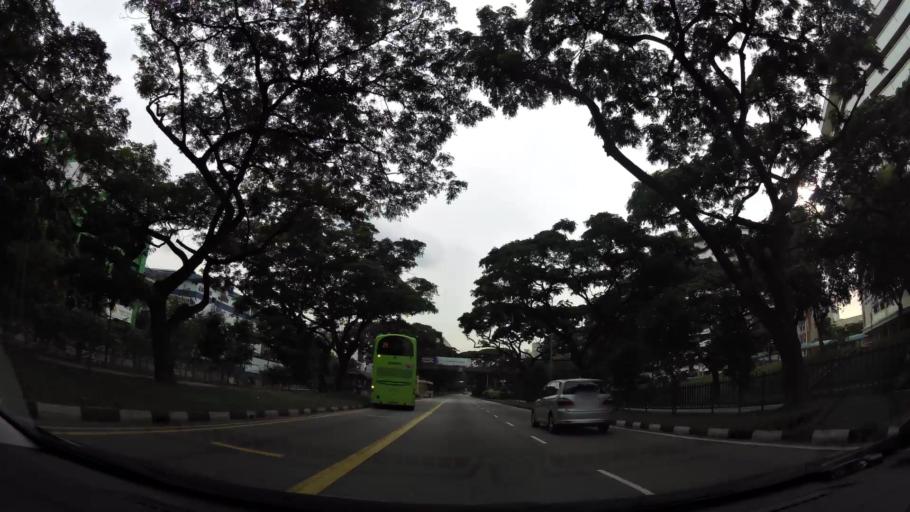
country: SG
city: Singapore
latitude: 1.3574
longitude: 103.8927
